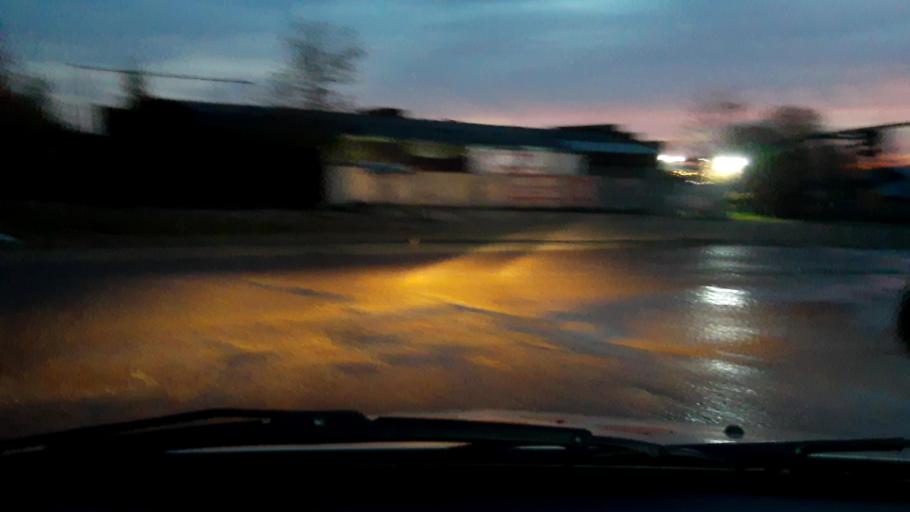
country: RU
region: Bashkortostan
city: Ufa
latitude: 54.8348
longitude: 56.0867
